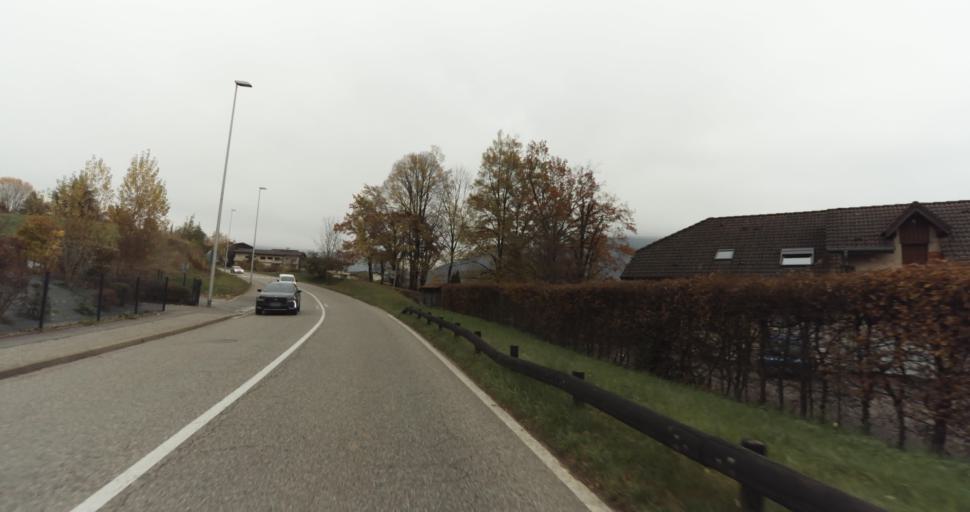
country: FR
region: Rhone-Alpes
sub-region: Departement de la Haute-Savoie
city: Annecy-le-Vieux
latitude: 45.9241
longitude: 6.1424
